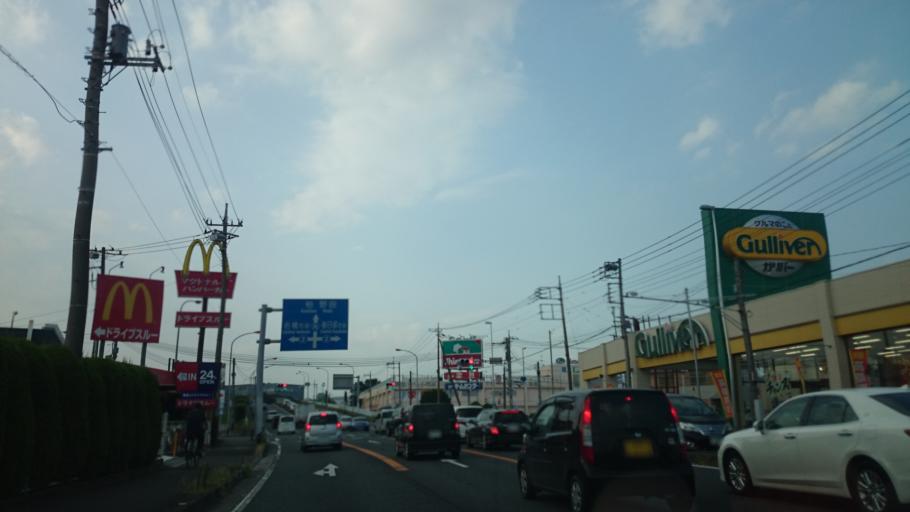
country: JP
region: Saitama
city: Kasukabe
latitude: 35.9718
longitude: 139.7365
